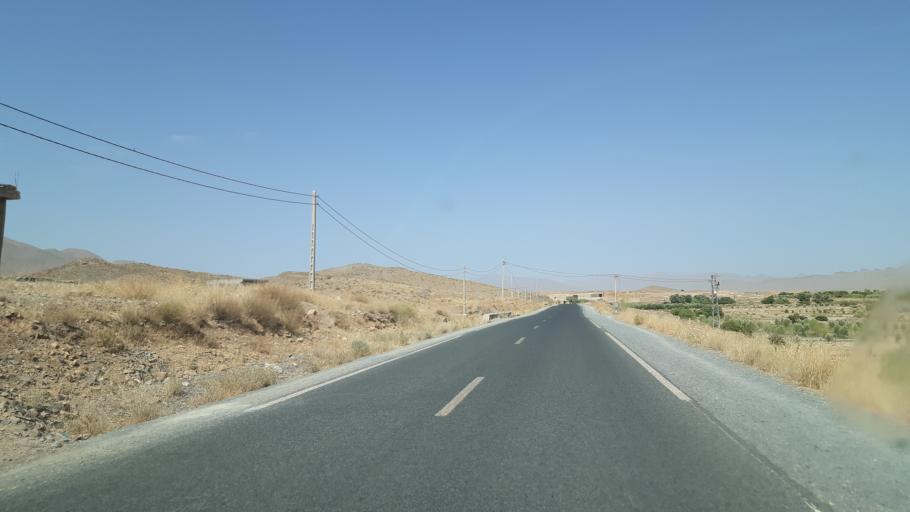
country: MA
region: Meknes-Tafilalet
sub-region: Errachidia
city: Amouguer
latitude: 32.2220
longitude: -4.6917
